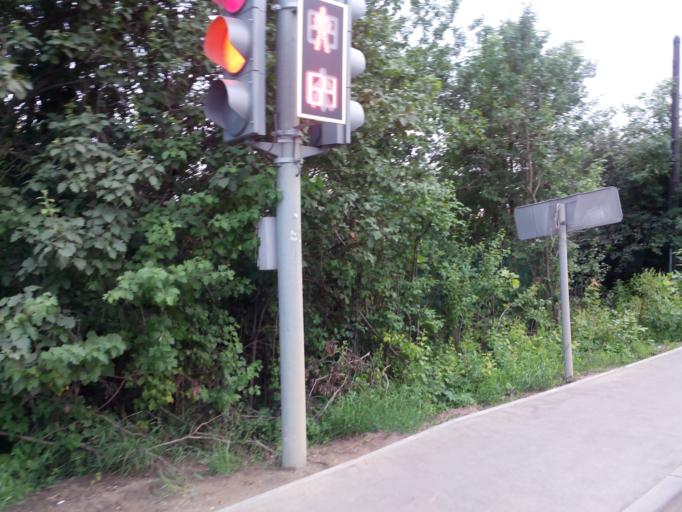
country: RU
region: Moskovskaya
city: Lesnoy Gorodok
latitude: 55.6587
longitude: 37.1855
